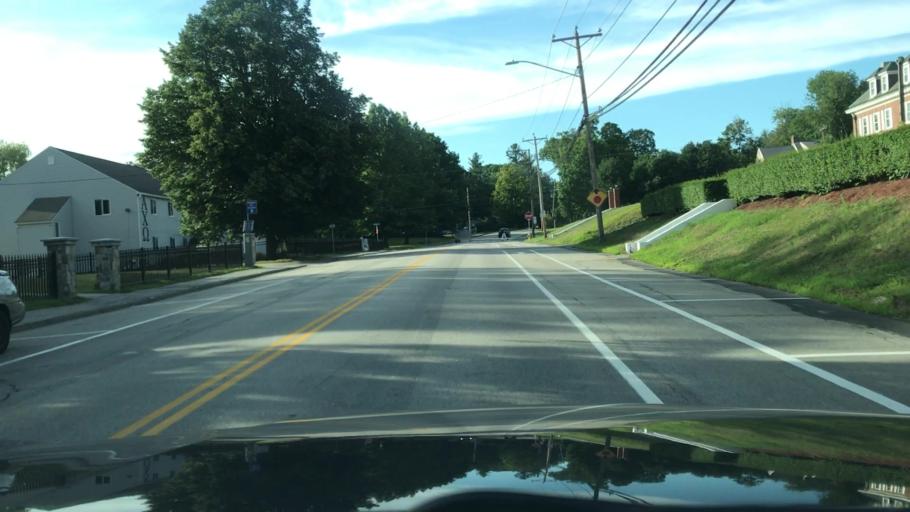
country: US
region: New Hampshire
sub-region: Strafford County
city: Durham
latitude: 43.1368
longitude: -70.9257
